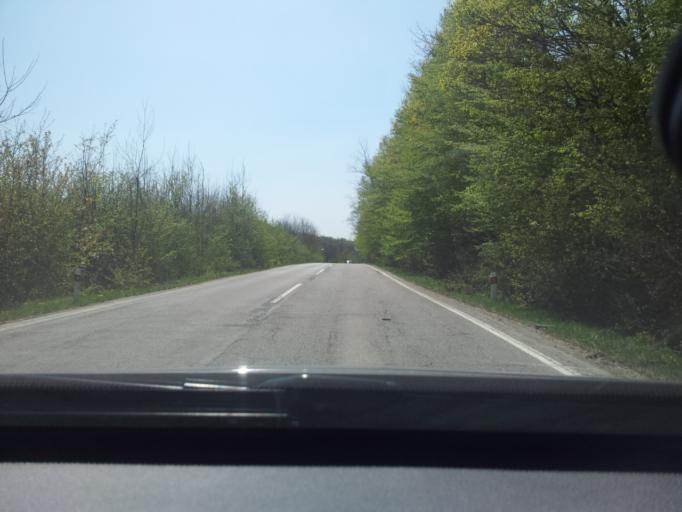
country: SK
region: Nitriansky
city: Zlate Moravce
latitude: 48.4674
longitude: 18.4121
